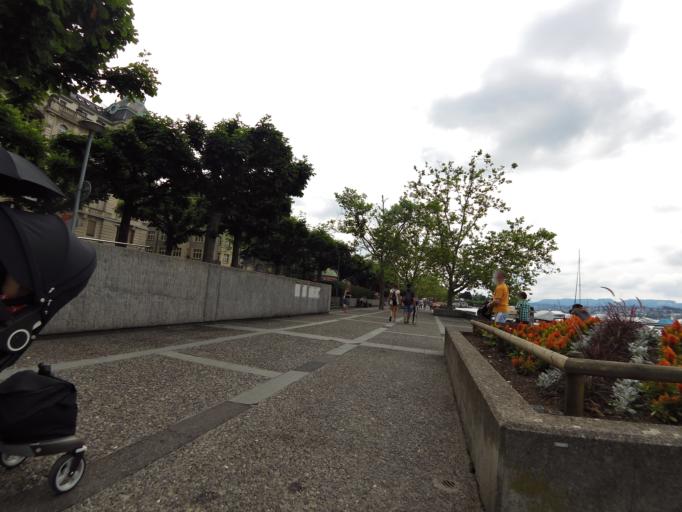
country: CH
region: Zurich
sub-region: Bezirk Zuerich
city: Zurich
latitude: 47.3641
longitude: 8.5457
